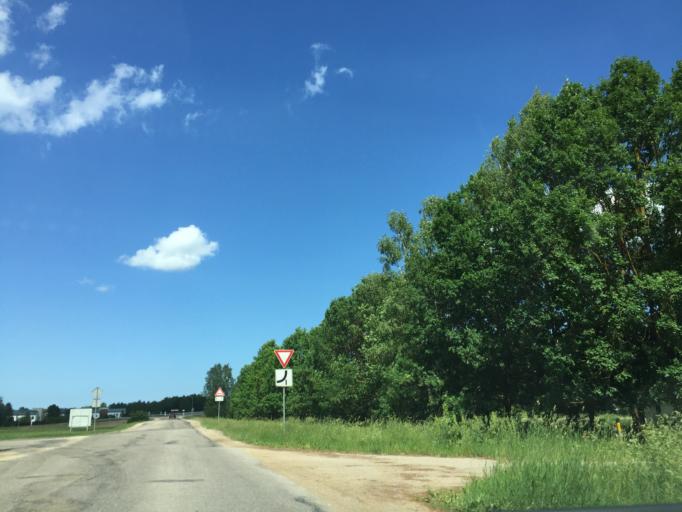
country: LV
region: Babite
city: Pinki
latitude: 56.8753
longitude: 23.9523
